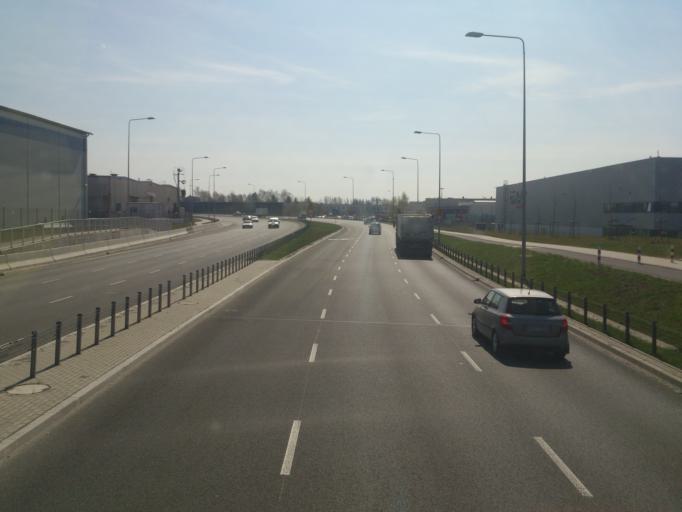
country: PL
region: Lodz Voivodeship
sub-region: Powiat lodzki wschodni
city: Starowa Gora
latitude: 51.7022
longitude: 19.4707
